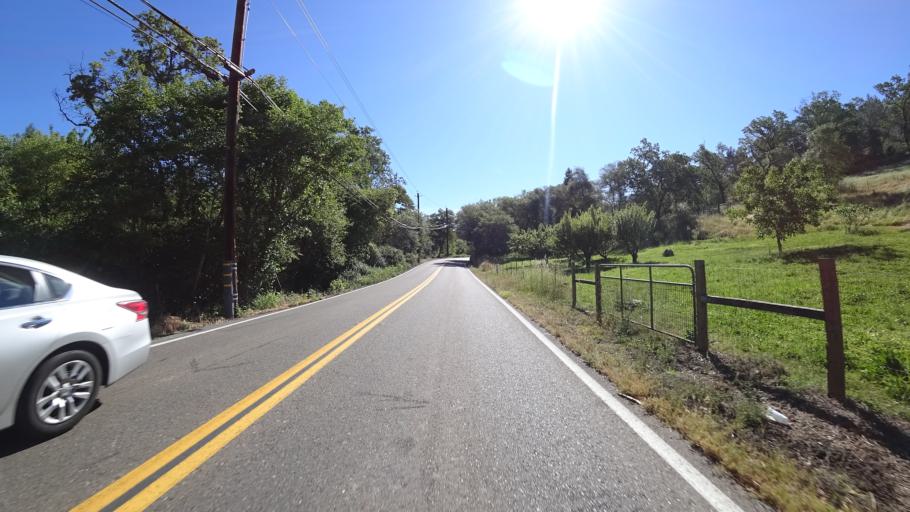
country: US
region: California
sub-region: Placer County
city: Newcastle
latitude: 38.8790
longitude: -121.1436
